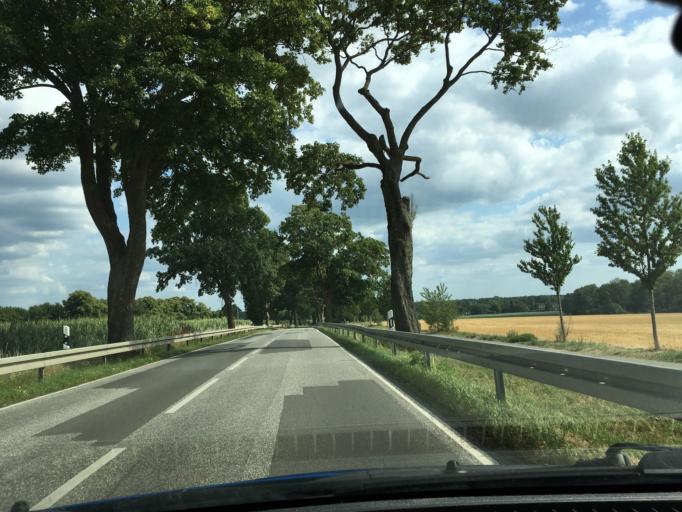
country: DE
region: Mecklenburg-Vorpommern
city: Lubtheen
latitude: 53.3760
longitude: 11.0831
